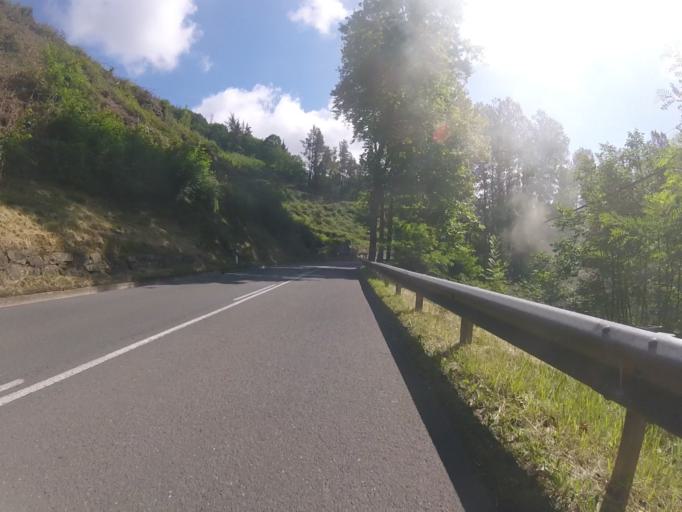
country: ES
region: Basque Country
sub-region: Provincia de Guipuzcoa
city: Azpeitia
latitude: 43.1785
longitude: -2.2486
